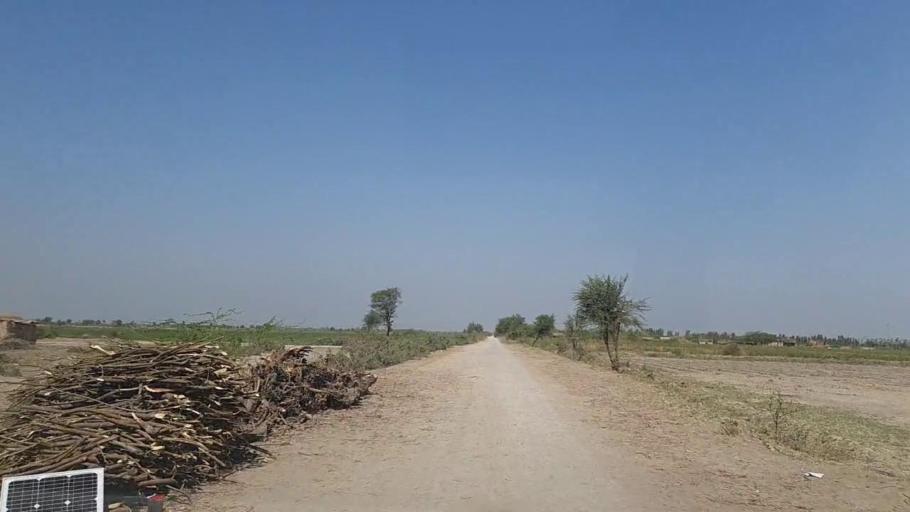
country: PK
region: Sindh
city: Samaro
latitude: 25.1981
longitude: 69.4041
